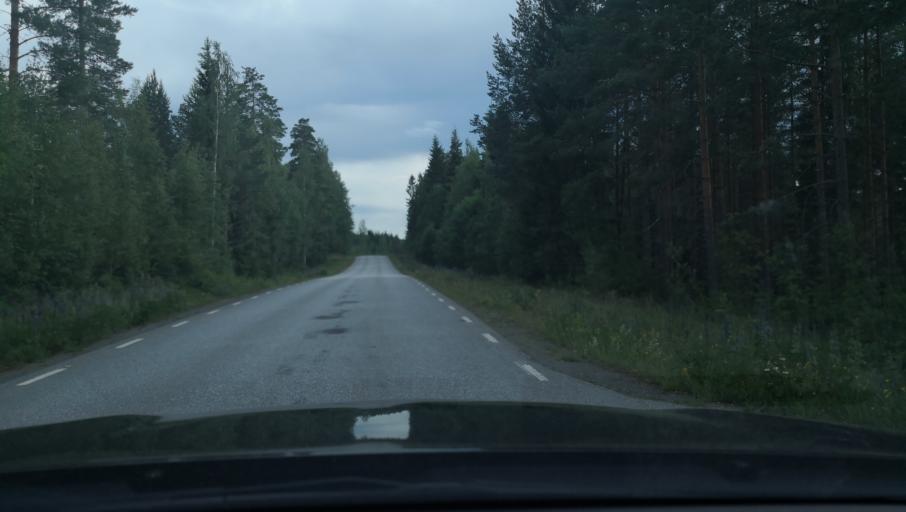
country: SE
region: Dalarna
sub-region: Smedjebackens Kommun
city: Smedjebacken
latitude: 60.0313
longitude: 15.5012
